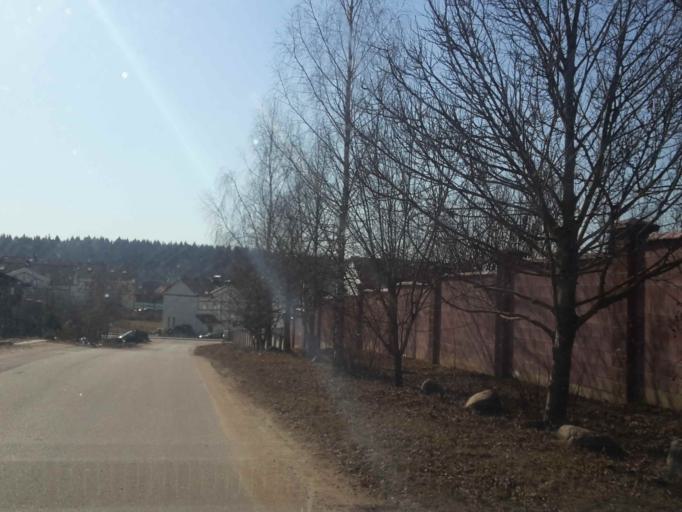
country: BY
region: Minsk
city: Zhdanovichy
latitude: 53.9161
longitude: 27.3972
